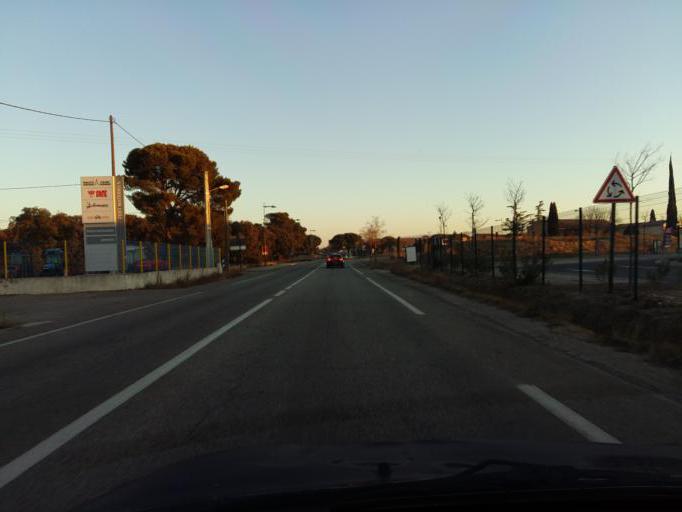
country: FR
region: Provence-Alpes-Cote d'Azur
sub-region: Departement du Vaucluse
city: Sainte-Cecile-les-Vignes
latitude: 44.2323
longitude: 4.8816
